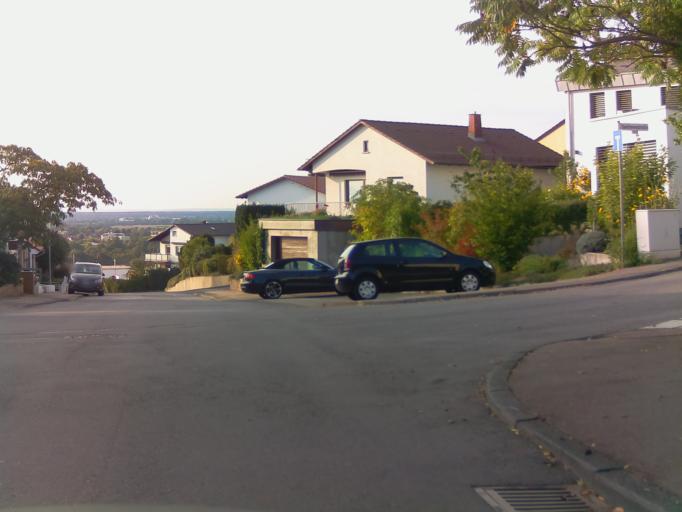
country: DE
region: Baden-Wuerttemberg
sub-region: Karlsruhe Region
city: Weinheim
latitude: 49.5374
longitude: 8.6646
